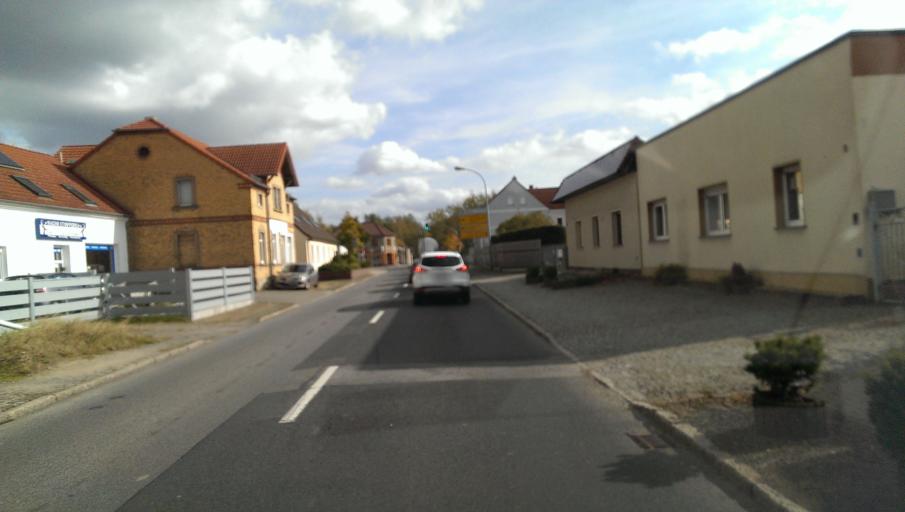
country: DE
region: Saxony
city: Bernsdorf
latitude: 51.3764
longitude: 14.0689
